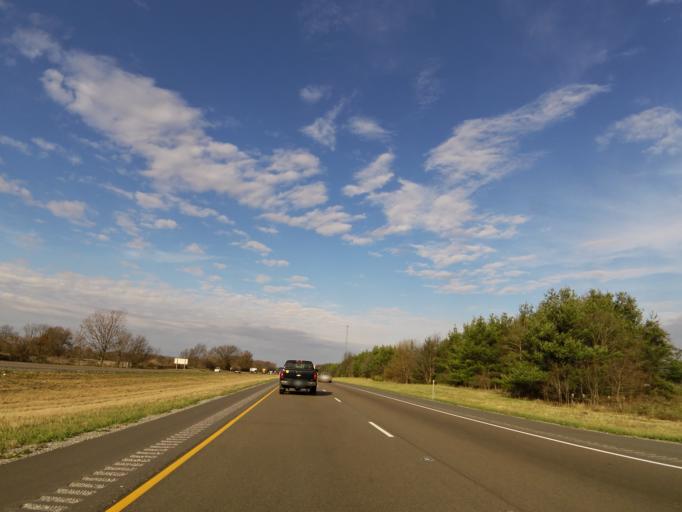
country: US
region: Illinois
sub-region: Washington County
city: Okawville
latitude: 38.4509
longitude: -89.5510
